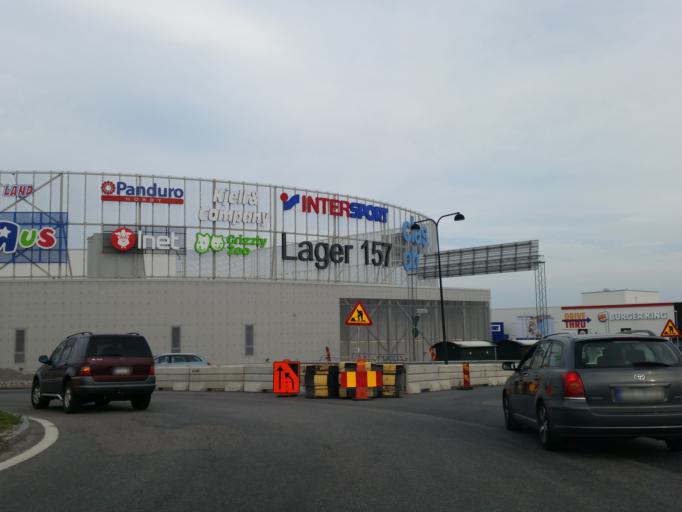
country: SE
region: Stockholm
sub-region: Jarfalla Kommun
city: Jakobsberg
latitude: 59.4126
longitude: 17.8598
